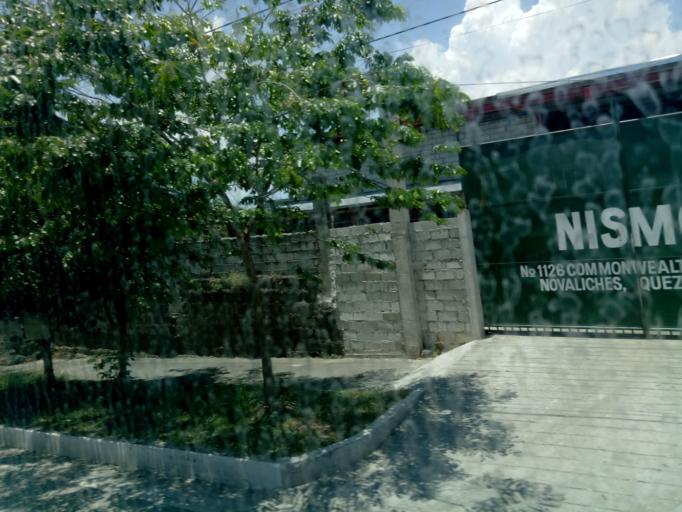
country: PH
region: Calabarzon
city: Bagong Pagasa
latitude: 14.7291
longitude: 121.0473
